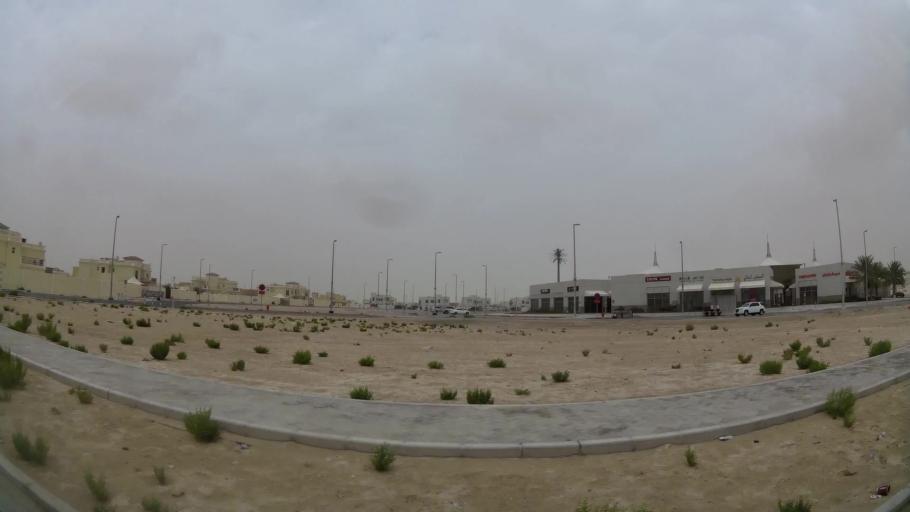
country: AE
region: Abu Dhabi
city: Abu Dhabi
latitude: 24.4425
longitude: 54.7405
